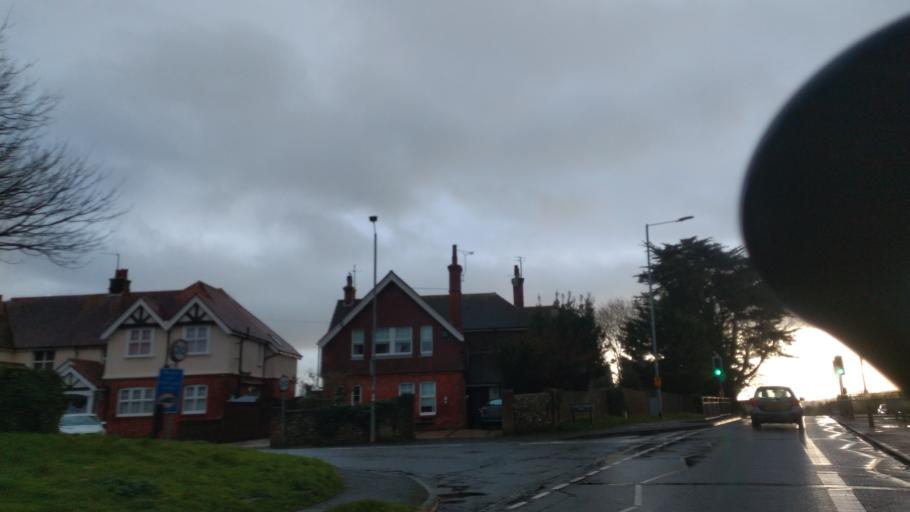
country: GB
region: England
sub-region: East Sussex
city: Eastbourne
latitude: 50.8002
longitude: 0.2551
